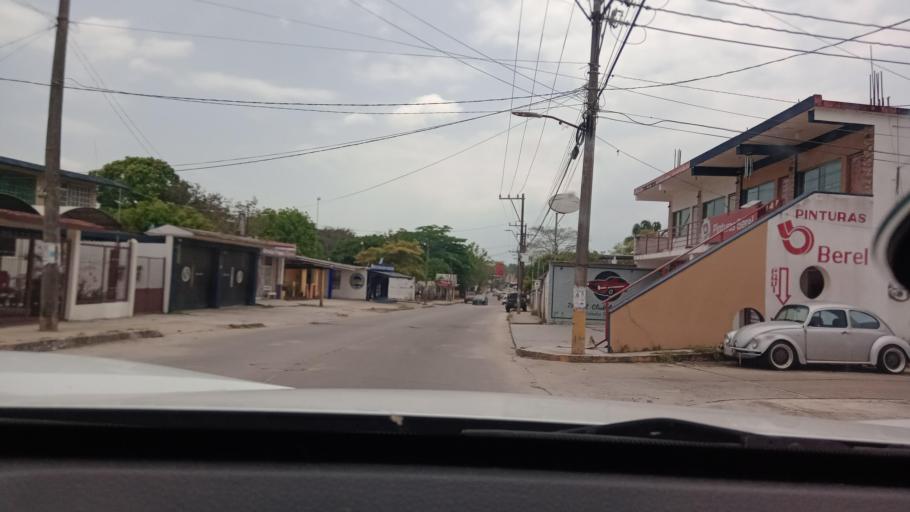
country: MX
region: Veracruz
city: Las Choapas
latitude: 17.9011
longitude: -94.0966
